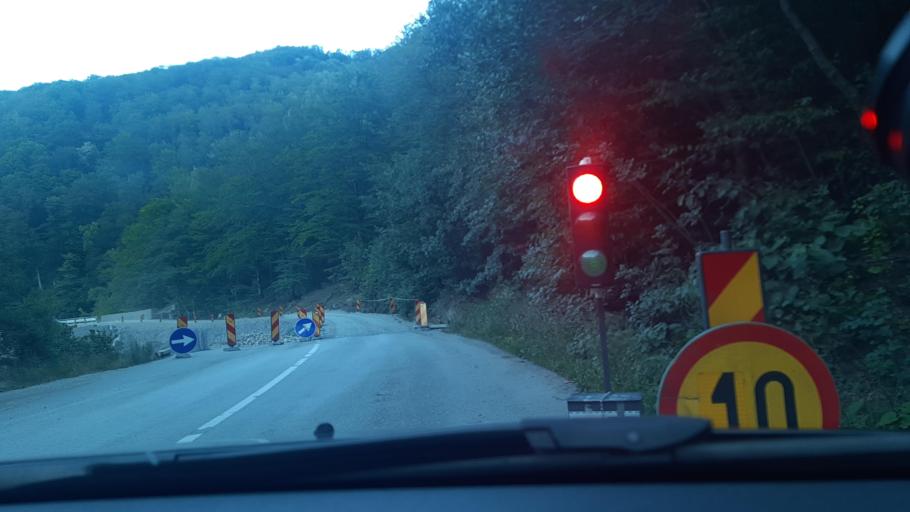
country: RO
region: Gorj
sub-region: Comuna Bumbesti-Jiu
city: Bumbesti-Jiu
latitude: 45.2549
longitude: 23.3882
